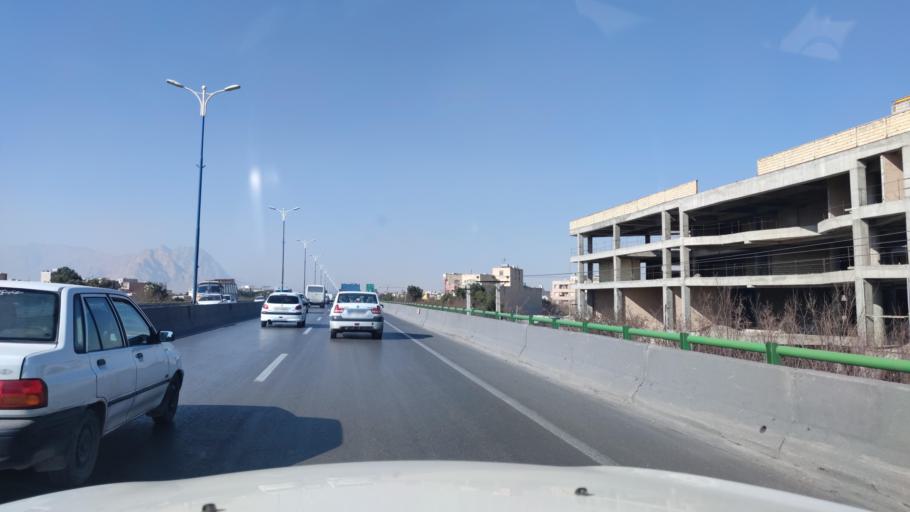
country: IR
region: Isfahan
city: Rehnan
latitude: 32.6985
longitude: 51.6196
